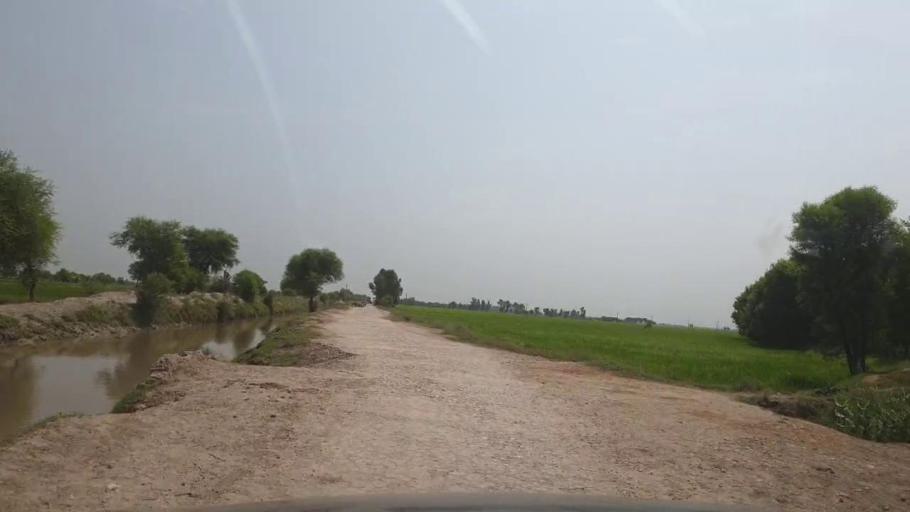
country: PK
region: Sindh
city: Ratodero
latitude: 27.8805
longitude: 68.3460
